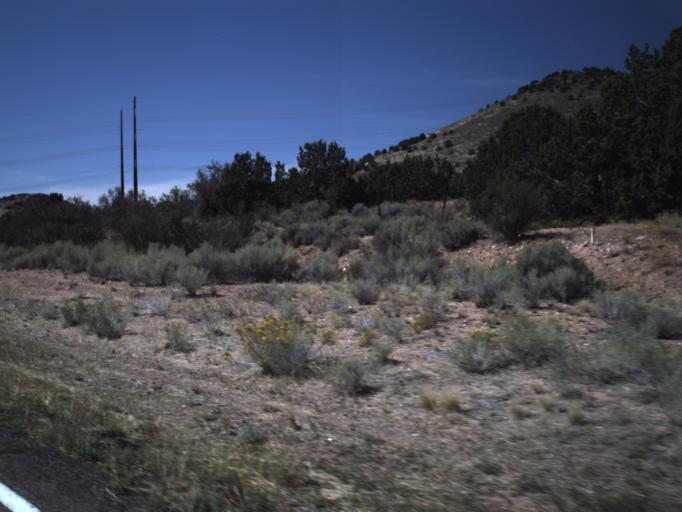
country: US
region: Utah
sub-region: Washington County
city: Enterprise
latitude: 37.4061
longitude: -113.6364
